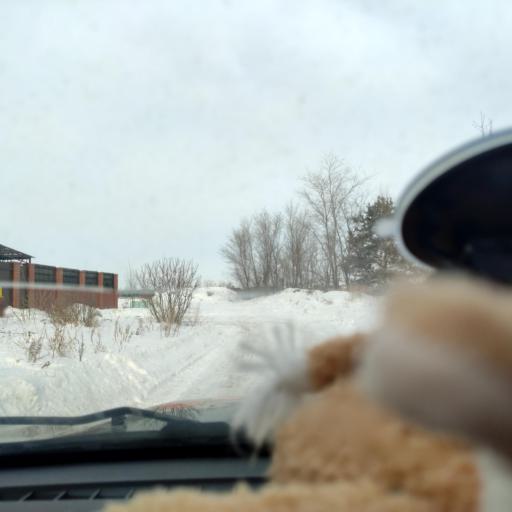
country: RU
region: Samara
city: Tol'yatti
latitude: 53.5572
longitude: 49.3727
